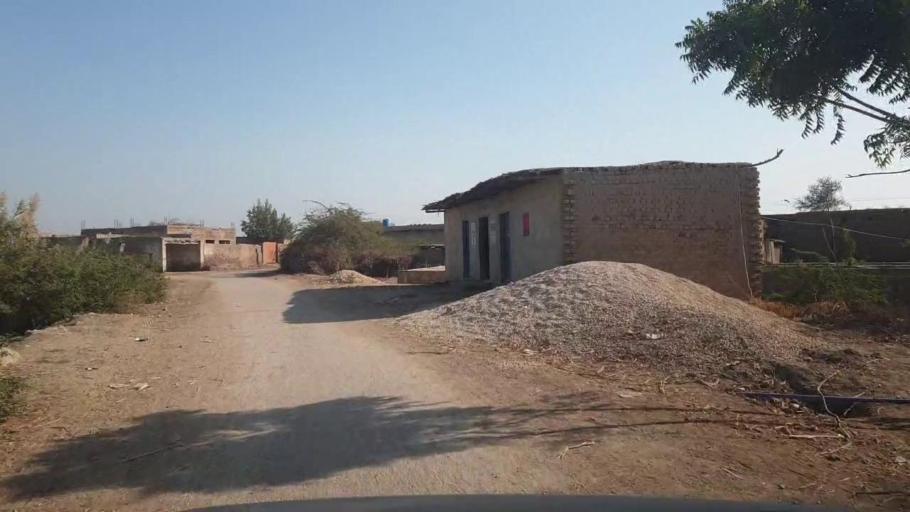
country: PK
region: Sindh
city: Chambar
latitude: 25.2883
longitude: 68.8525
